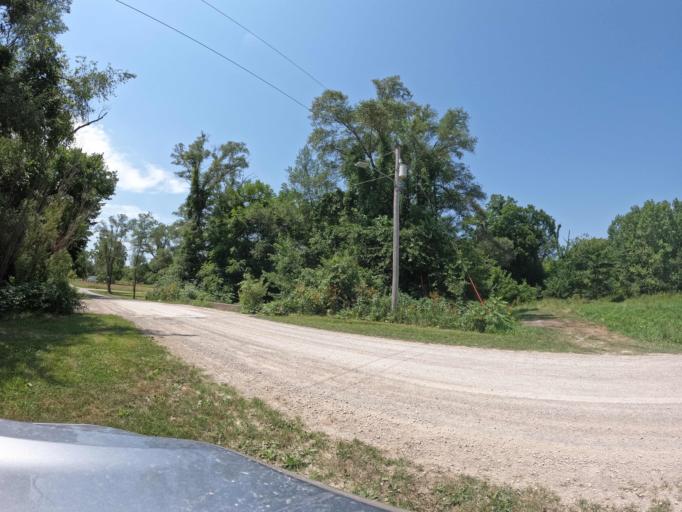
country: US
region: Iowa
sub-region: Appanoose County
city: Centerville
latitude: 40.7760
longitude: -92.9493
